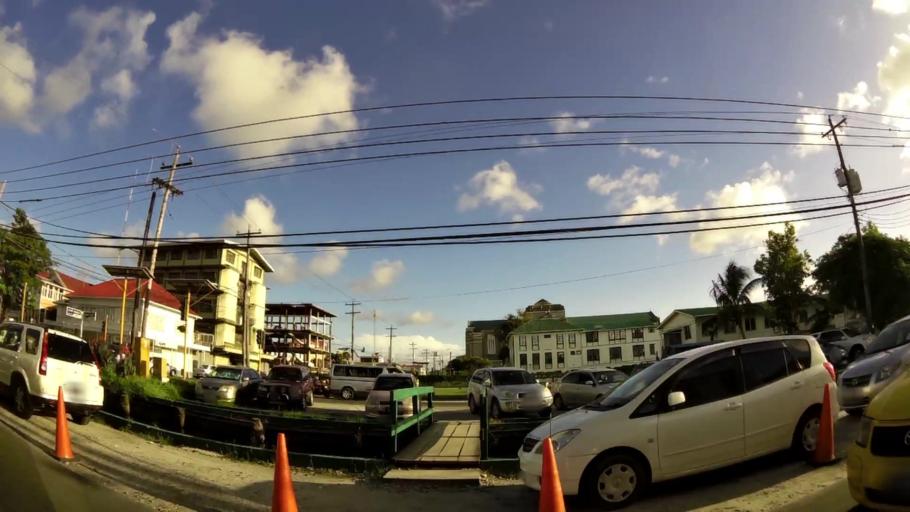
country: GY
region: Demerara-Mahaica
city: Georgetown
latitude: 6.8087
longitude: -58.1614
